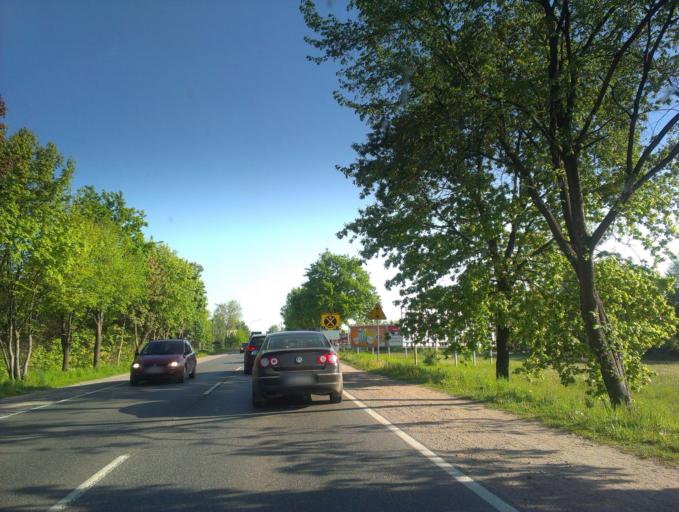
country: PL
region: Masovian Voivodeship
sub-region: Powiat piaseczynski
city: Piaseczno
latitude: 52.0742
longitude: 21.0356
